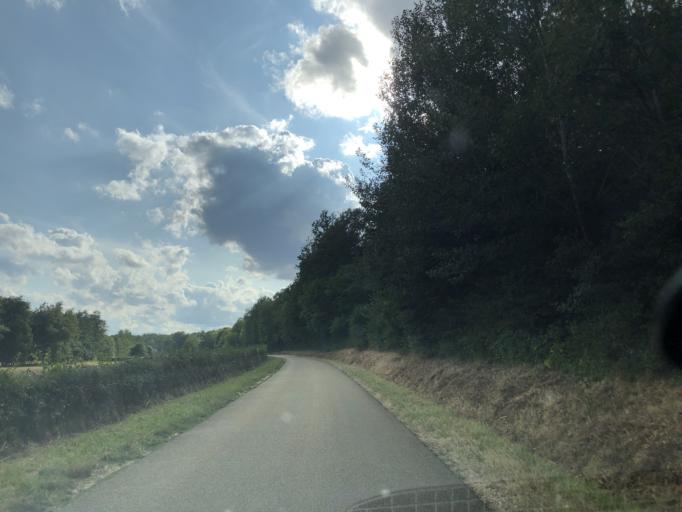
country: FR
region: Bourgogne
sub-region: Departement de l'Yonne
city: Saint-Georges-sur-Baulche
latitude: 47.8227
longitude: 3.5144
